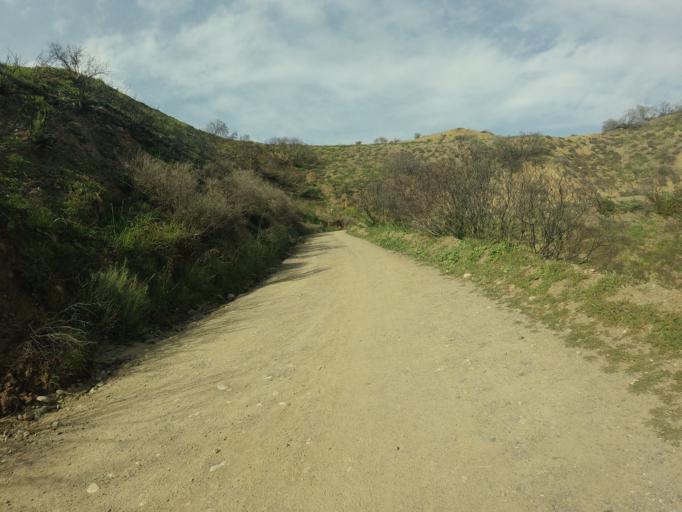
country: US
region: California
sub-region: Riverside County
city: Corona
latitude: 33.8383
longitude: -117.6092
